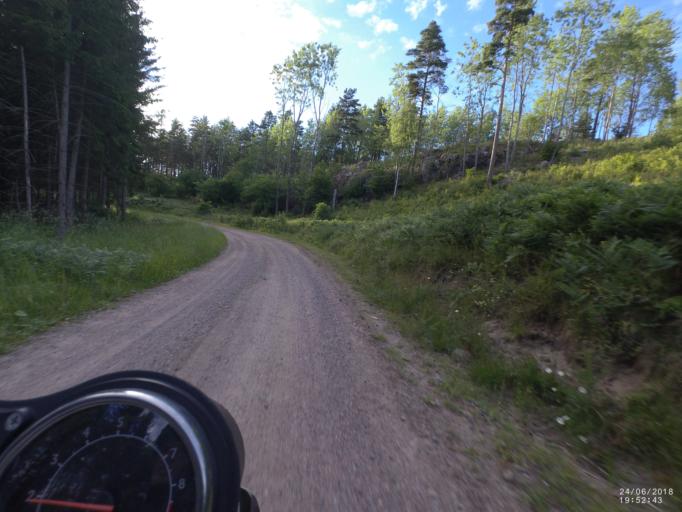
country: SE
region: Soedermanland
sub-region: Oxelosunds Kommun
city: Oxelosund
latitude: 58.7738
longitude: 17.1514
